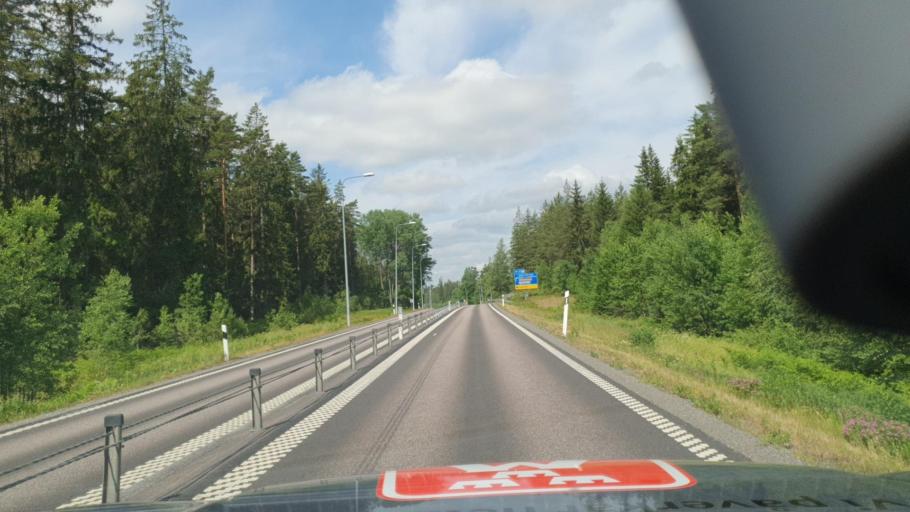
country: SE
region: Kalmar
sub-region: Emmaboda Kommun
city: Emmaboda
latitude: 56.7182
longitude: 15.6910
